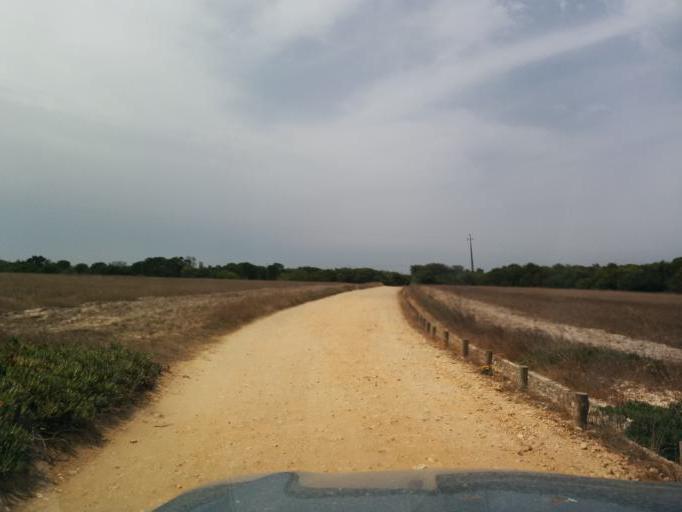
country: PT
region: Beja
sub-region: Odemira
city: Vila Nova de Milfontes
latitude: 37.7155
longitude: -8.7807
